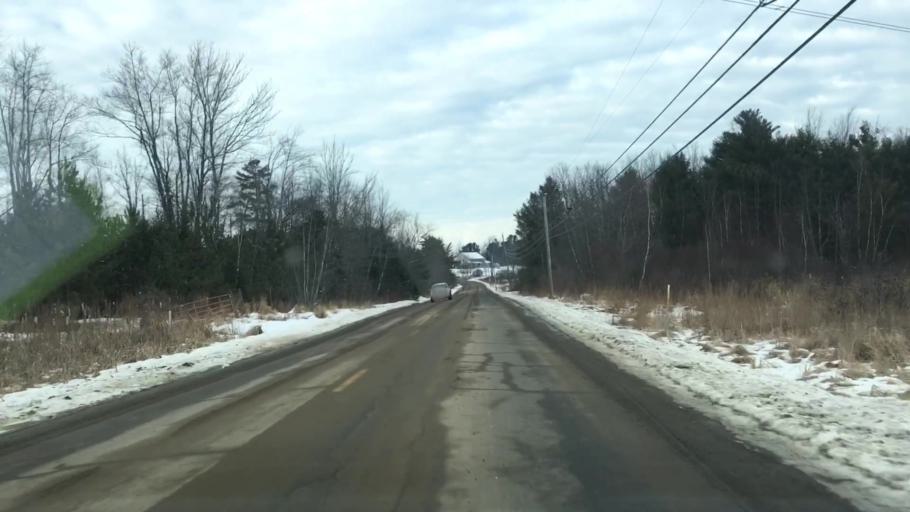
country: US
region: Maine
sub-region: Lincoln County
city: Whitefield
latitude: 44.2324
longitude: -69.6159
